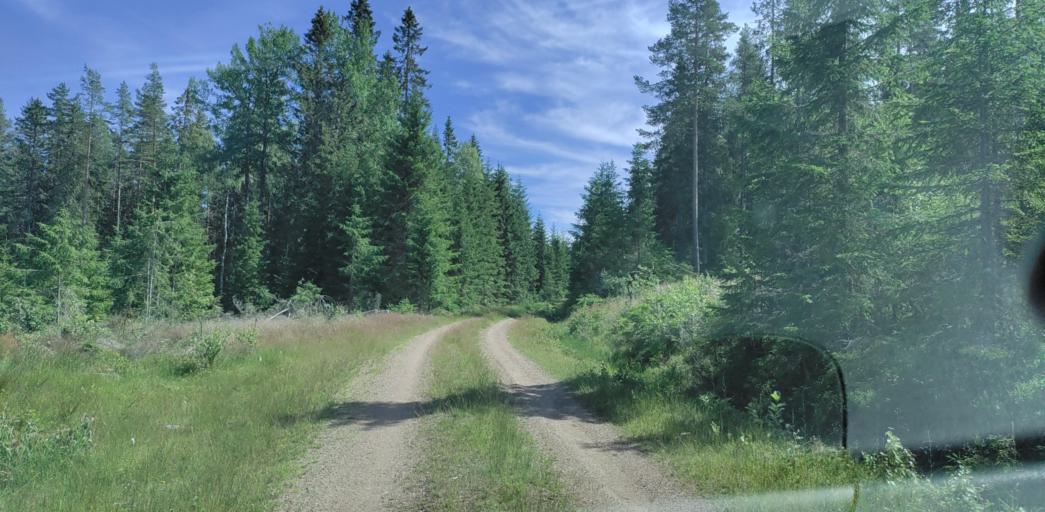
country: SE
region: Vaermland
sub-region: Hagfors Kommun
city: Ekshaerad
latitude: 60.0932
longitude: 13.3751
